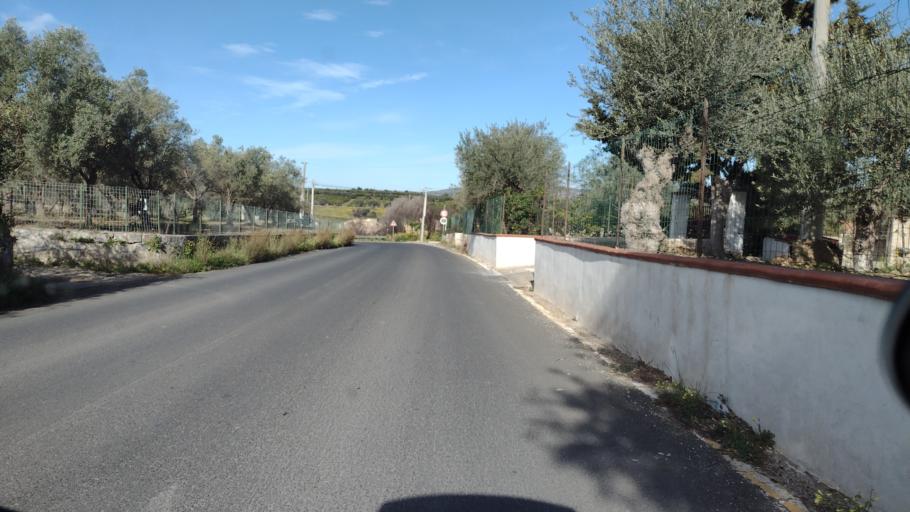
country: IT
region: Sicily
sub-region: Provincia di Siracusa
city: Noto
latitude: 36.8760
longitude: 15.1092
